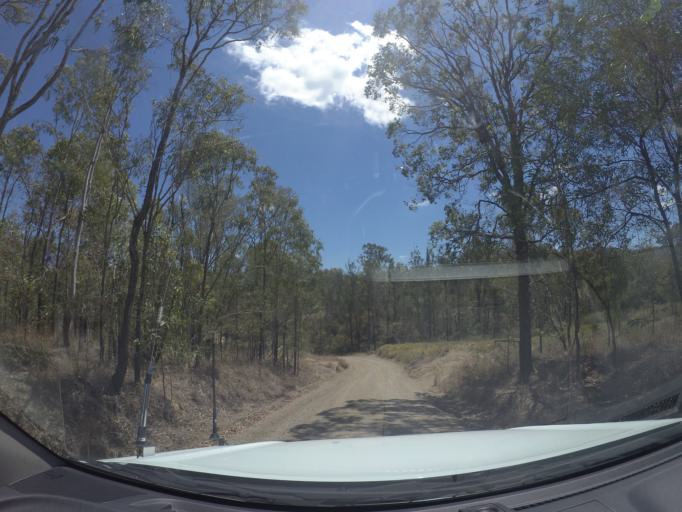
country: AU
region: Queensland
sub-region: Ipswich
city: Springfield Lakes
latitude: -27.8133
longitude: 152.8510
